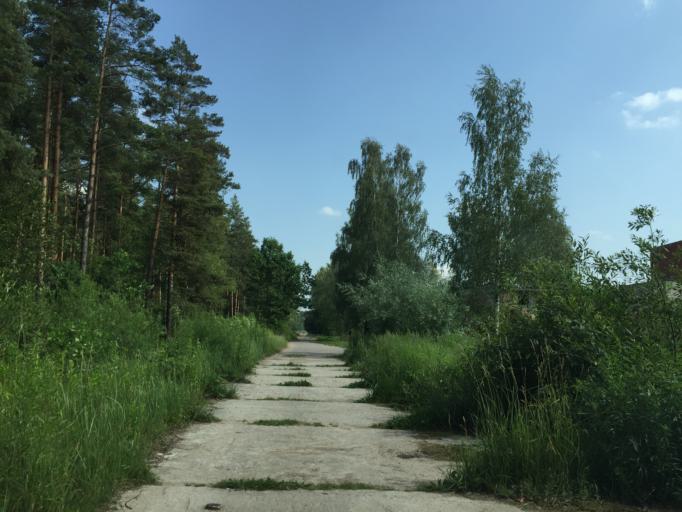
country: LV
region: Ozolnieku
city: Ozolnieki
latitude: 56.6742
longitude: 23.7613
